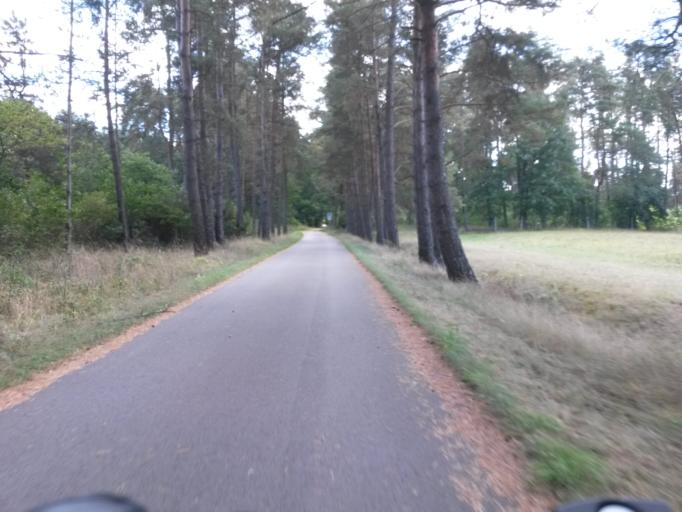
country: DE
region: Brandenburg
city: Templin
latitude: 53.1738
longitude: 13.5161
